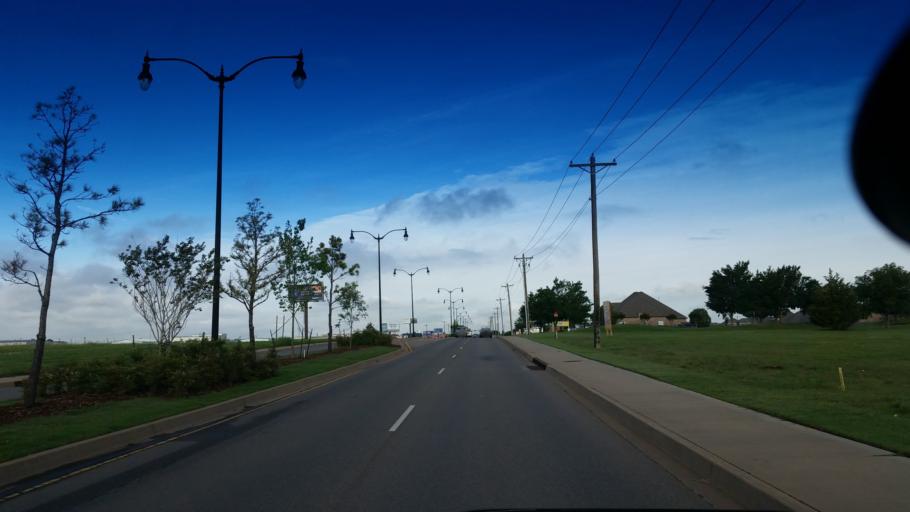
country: US
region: Oklahoma
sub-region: Oklahoma County
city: Edmond
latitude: 35.6237
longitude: -97.4991
